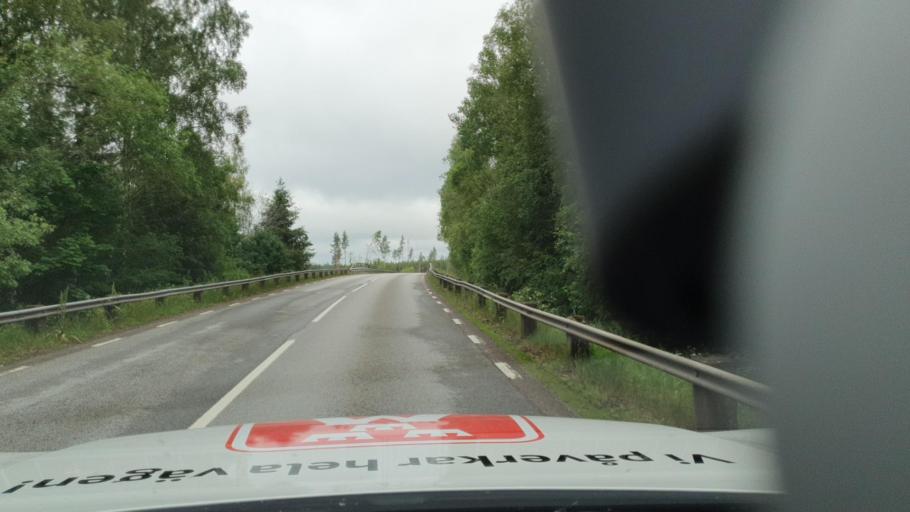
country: SE
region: Vaermland
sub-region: Kristinehamns Kommun
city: Bjorneborg
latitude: 59.1115
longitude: 14.2194
